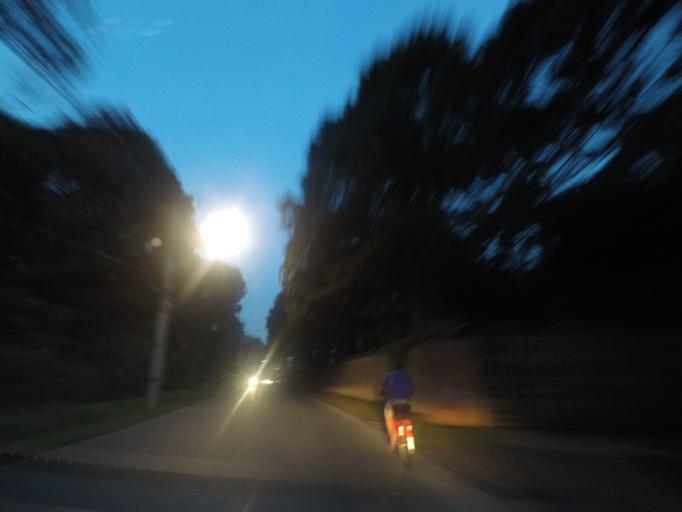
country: BR
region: Parana
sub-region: Pinhais
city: Pinhais
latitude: -25.4666
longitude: -49.1484
